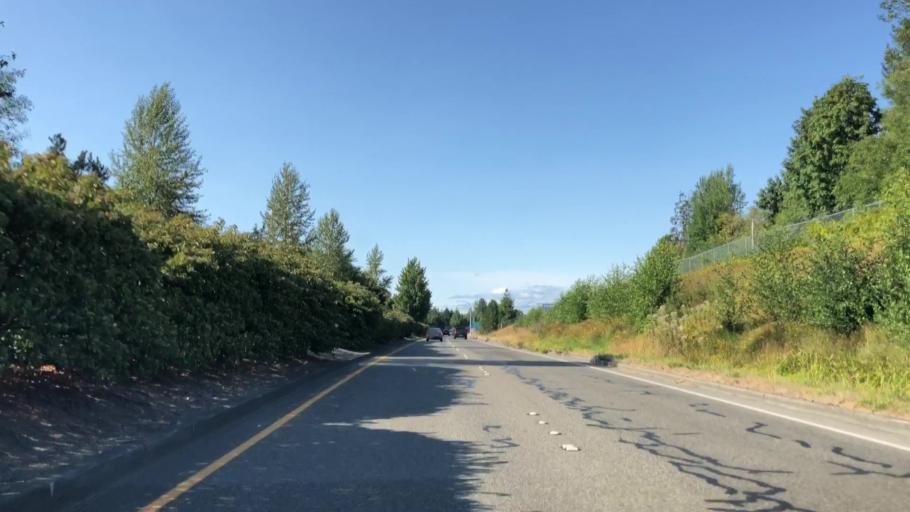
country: US
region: Washington
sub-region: Snohomish County
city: Mukilteo
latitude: 47.9150
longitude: -122.2924
